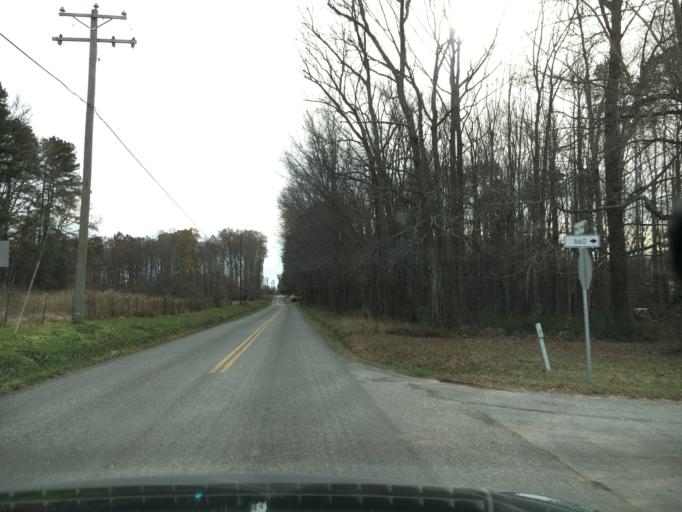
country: US
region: Virginia
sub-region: Henrico County
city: Wyndham
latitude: 37.6967
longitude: -77.6832
